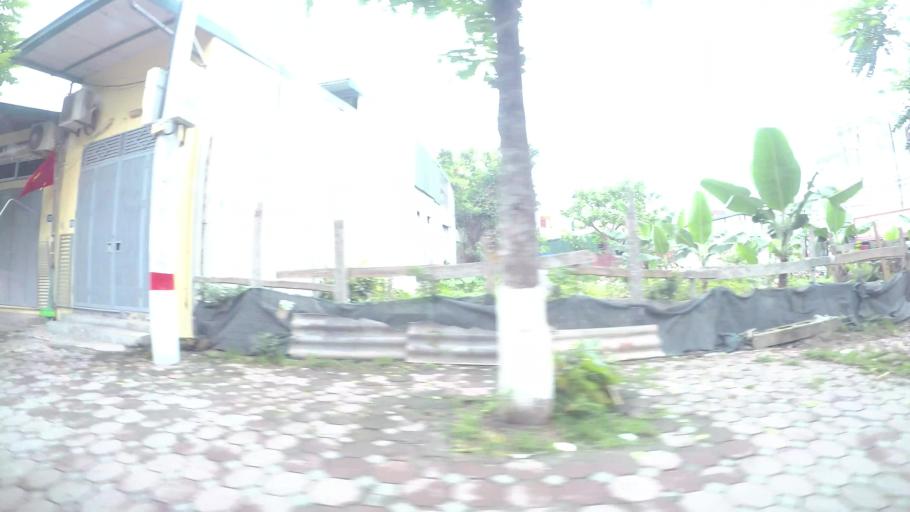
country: VN
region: Ha Noi
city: Van Dien
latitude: 20.9734
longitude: 105.8485
